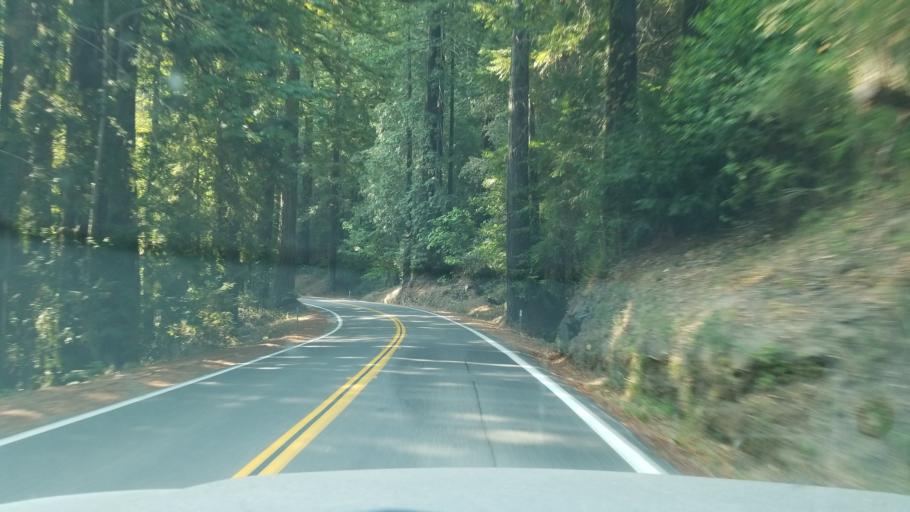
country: US
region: California
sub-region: Humboldt County
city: Redway
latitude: 40.2569
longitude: -123.8257
